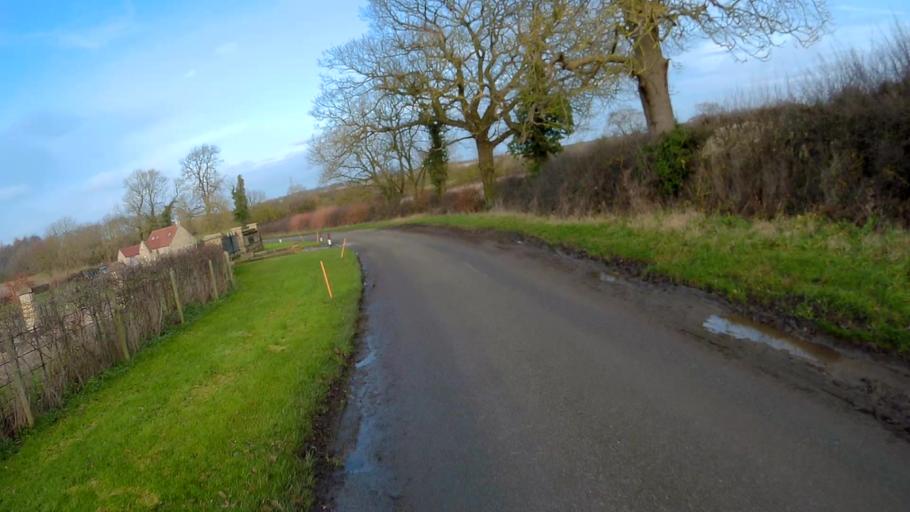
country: GB
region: England
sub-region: Lincolnshire
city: Bourne
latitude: 52.7523
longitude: -0.4160
